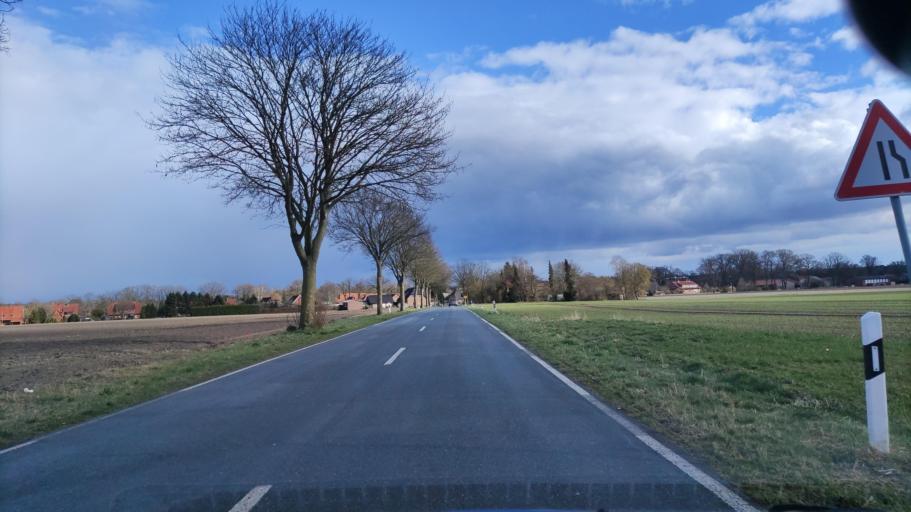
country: DE
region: Lower Saxony
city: Hermannsburg
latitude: 52.8025
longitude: 10.0797
